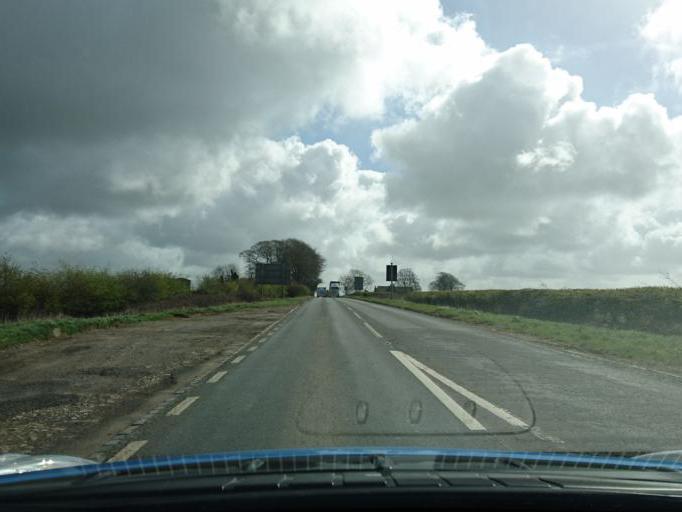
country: GB
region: England
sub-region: South Gloucestershire
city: Cold Ashton
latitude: 51.4523
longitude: -2.3849
